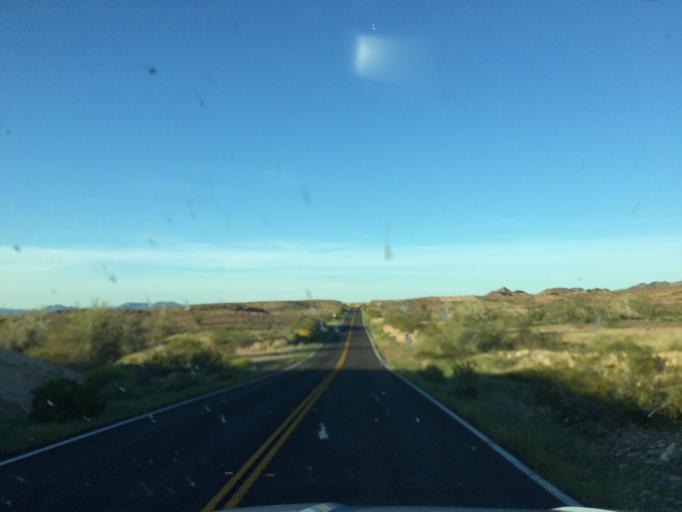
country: US
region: California
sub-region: Riverside County
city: Mesa Verde
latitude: 33.1878
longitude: -114.8624
